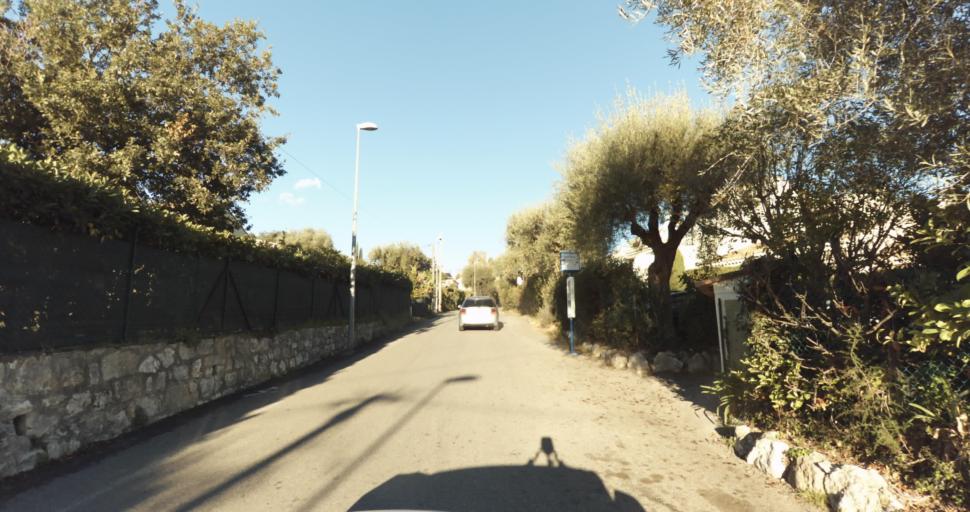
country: FR
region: Provence-Alpes-Cote d'Azur
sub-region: Departement des Alpes-Maritimes
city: Vence
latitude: 43.7181
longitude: 7.1269
